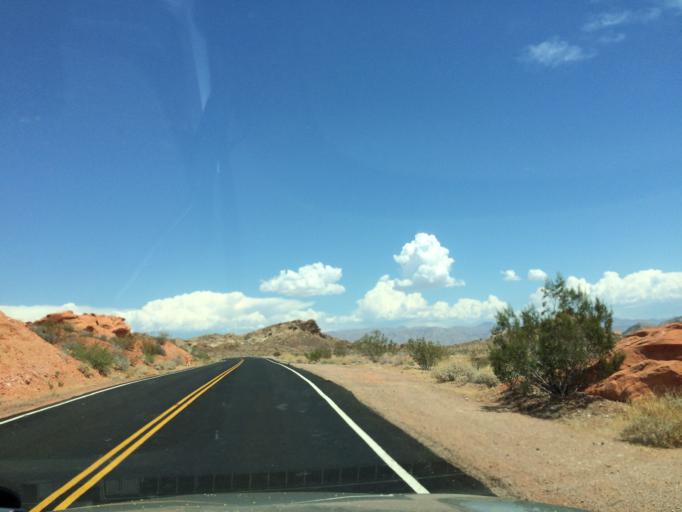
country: US
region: Nevada
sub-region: Clark County
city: Moapa Valley
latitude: 36.4257
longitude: -114.4855
